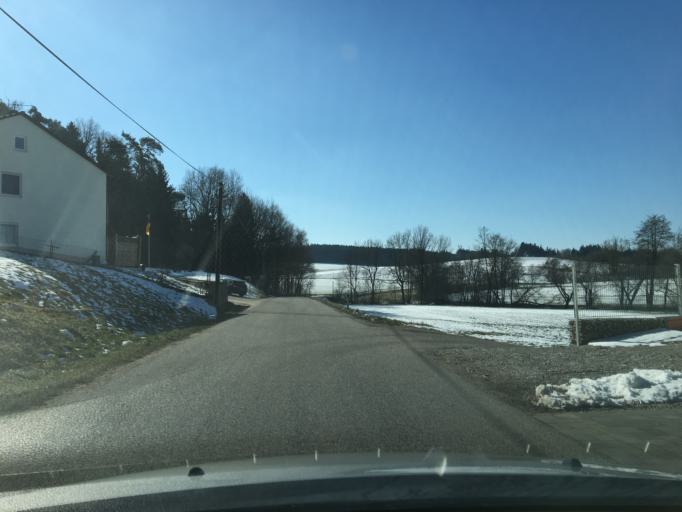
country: DE
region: Bavaria
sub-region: Lower Bavaria
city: Eching
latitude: 48.4924
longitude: 12.0662
